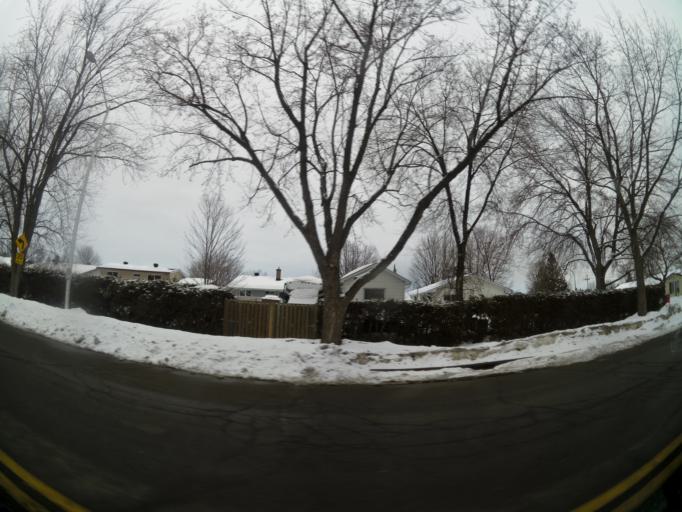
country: CA
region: Quebec
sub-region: Outaouais
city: Gatineau
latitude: 45.4611
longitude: -75.6027
